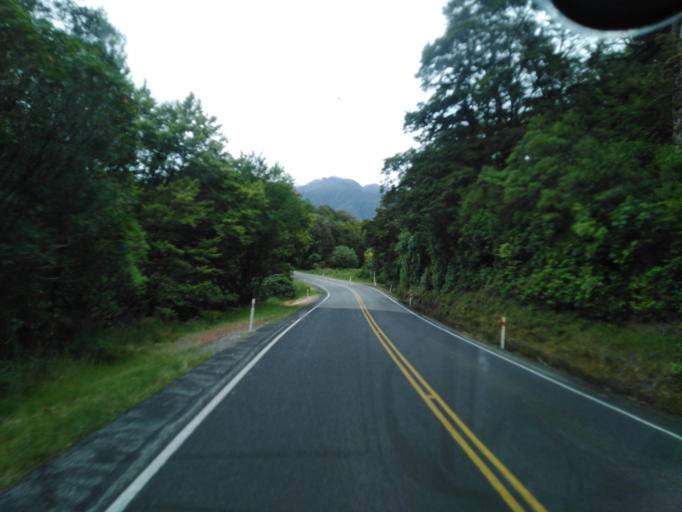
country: NZ
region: Tasman
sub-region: Tasman District
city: Wakefield
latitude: -41.7091
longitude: 172.5808
